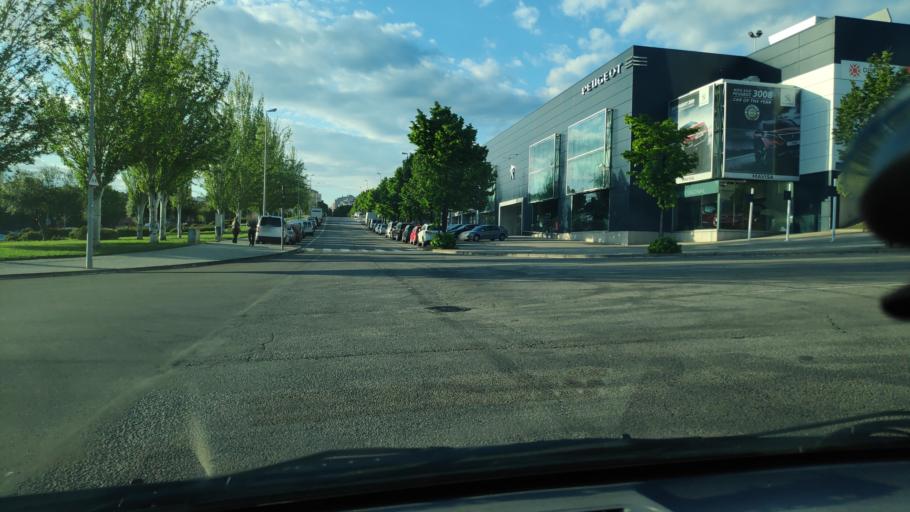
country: ES
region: Catalonia
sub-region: Provincia de Barcelona
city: Terrassa
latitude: 41.5486
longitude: 2.0232
